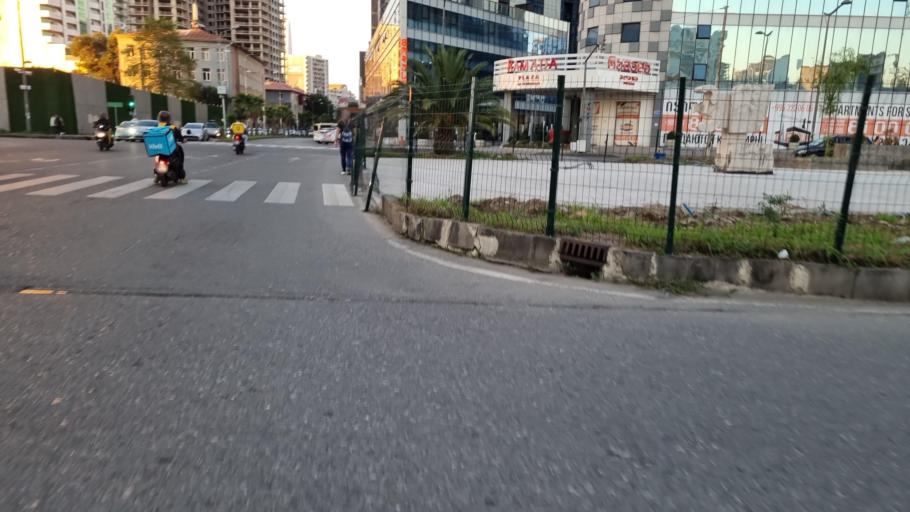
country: GE
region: Ajaria
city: Batumi
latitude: 41.6391
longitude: 41.6159
